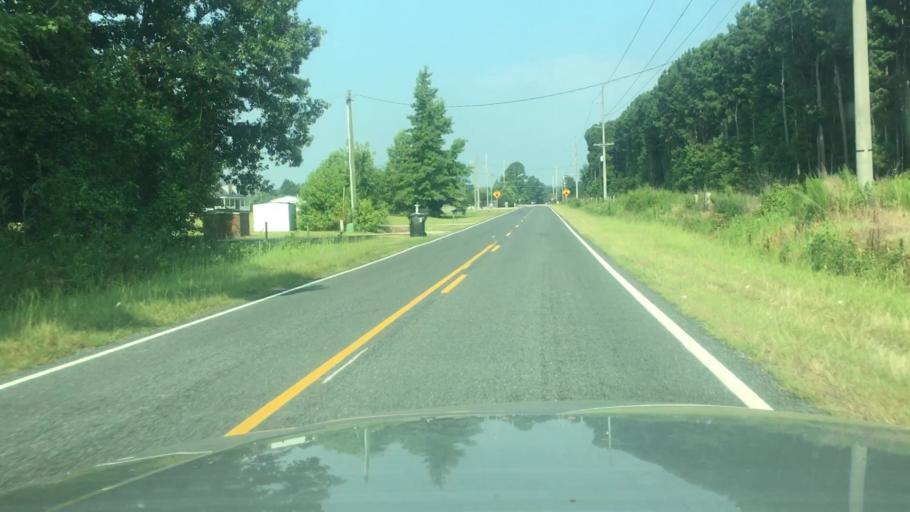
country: US
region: North Carolina
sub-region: Cumberland County
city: Hope Mills
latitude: 34.8984
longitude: -78.8957
